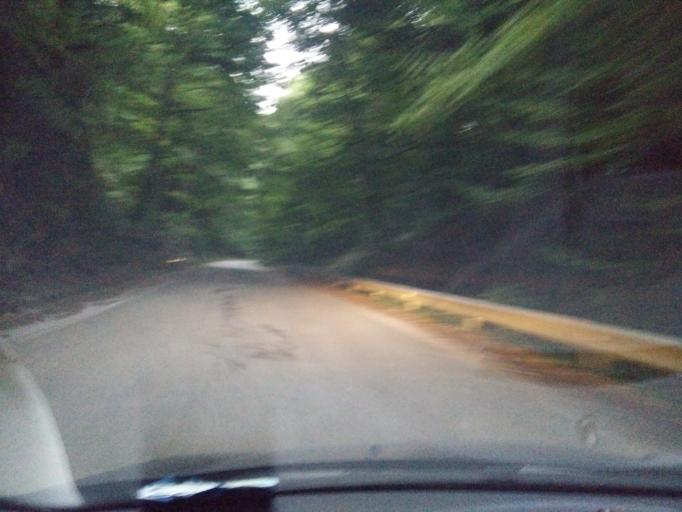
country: IT
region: Apulia
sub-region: Provincia di Foggia
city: Vico del Gargano
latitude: 41.8332
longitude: 16.0375
